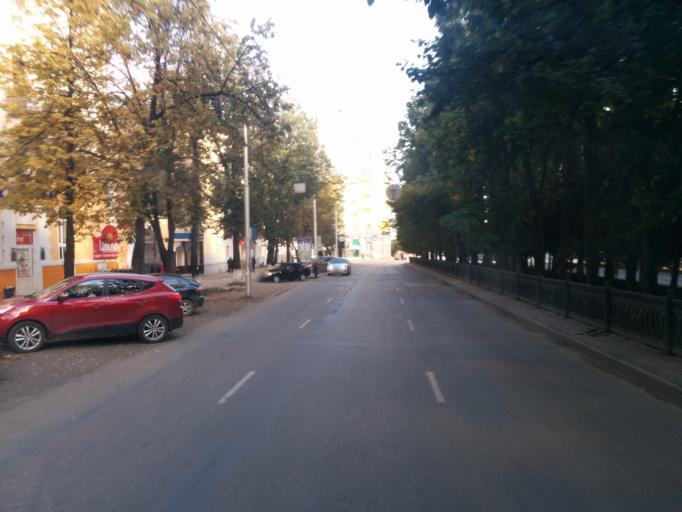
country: RU
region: Bashkortostan
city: Ufa
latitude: 54.8182
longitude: 56.0735
